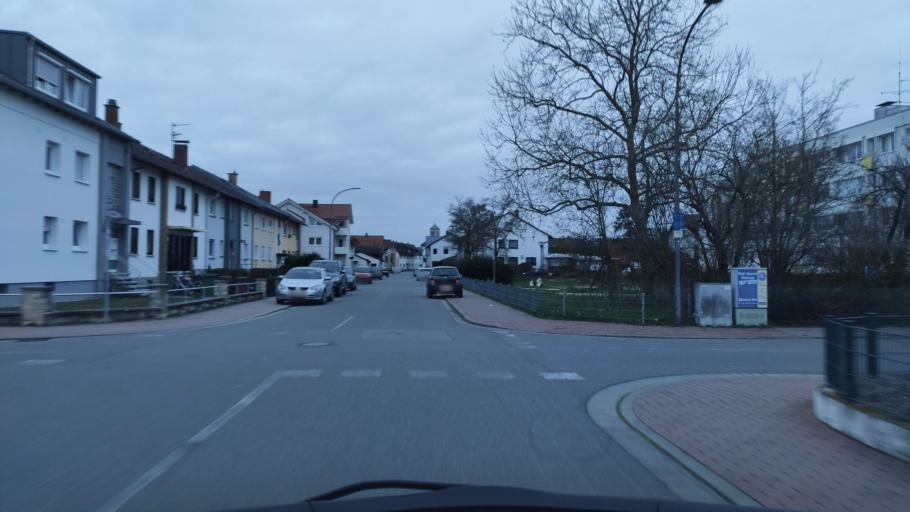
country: DE
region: Baden-Wuerttemberg
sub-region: Karlsruhe Region
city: Hockenheim
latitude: 49.3149
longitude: 8.5586
